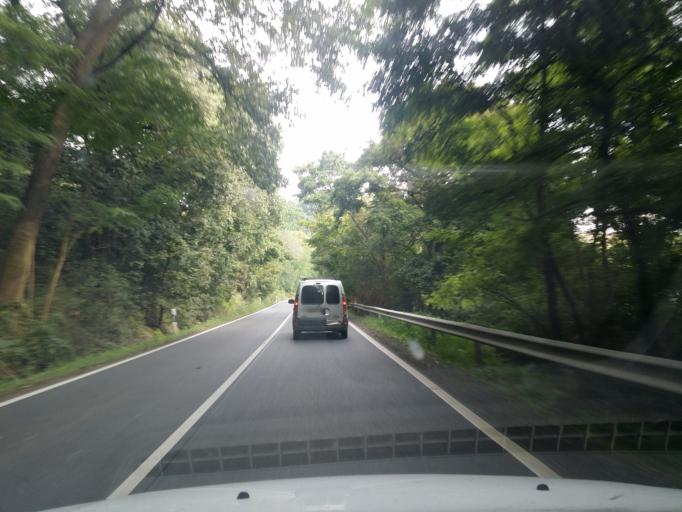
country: HU
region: Pest
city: Acsa
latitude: 47.7895
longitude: 19.3650
